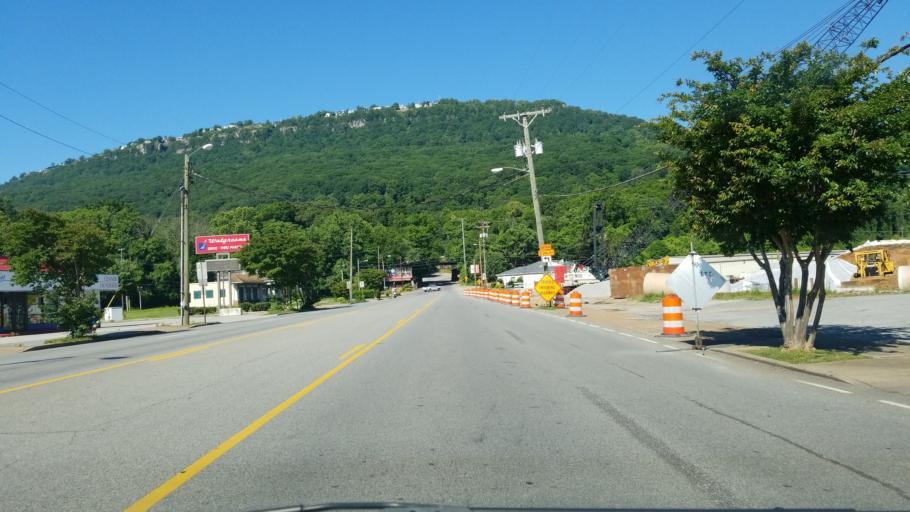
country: US
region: Tennessee
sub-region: Hamilton County
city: Lookout Mountain
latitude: 35.0144
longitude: -85.3255
